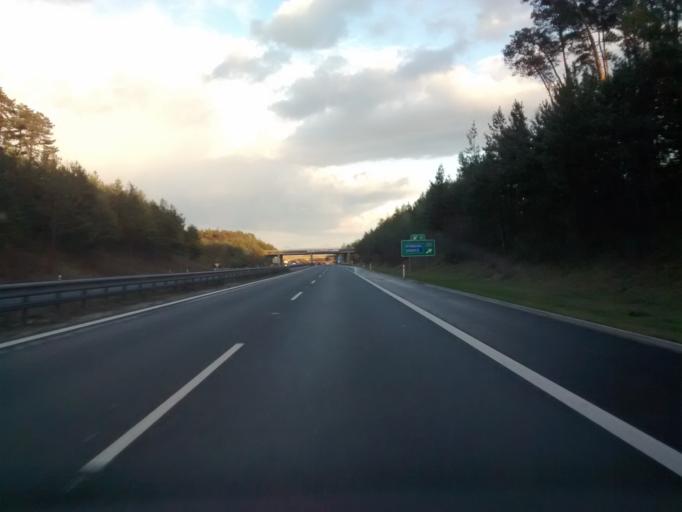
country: CZ
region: Central Bohemia
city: Poricany
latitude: 50.1202
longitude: 14.9382
